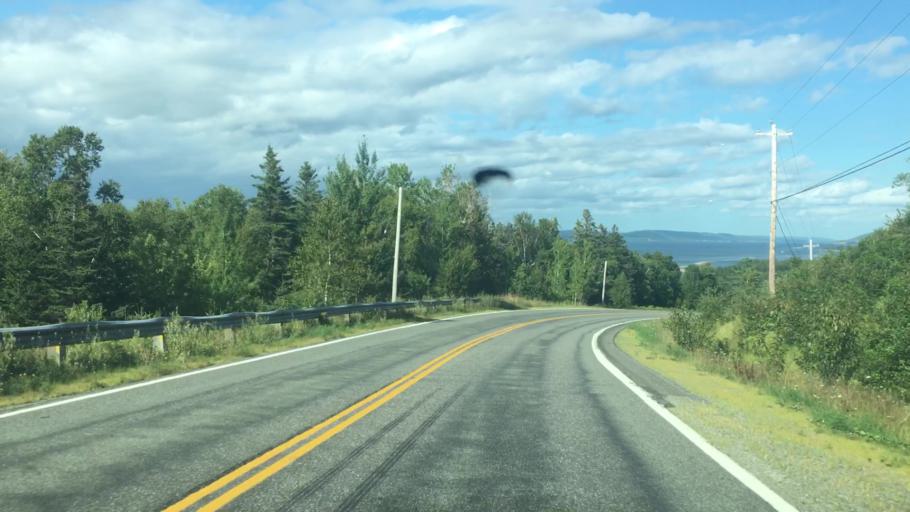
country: CA
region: Nova Scotia
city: Sydney
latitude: 45.8653
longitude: -60.6223
